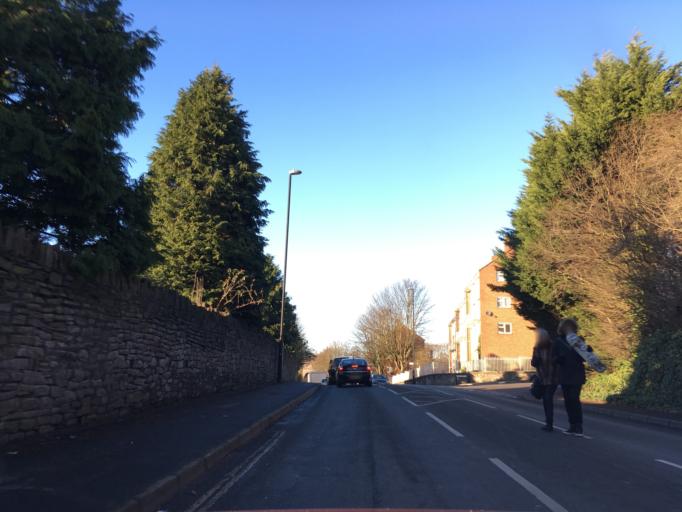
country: GB
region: England
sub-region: South Gloucestershire
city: Kingswood
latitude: 51.4692
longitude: -2.5501
